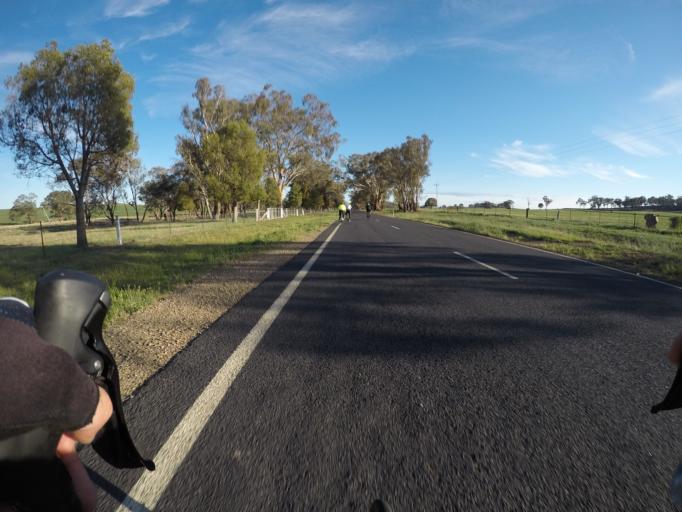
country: AU
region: New South Wales
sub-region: Cabonne
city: Molong
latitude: -32.9478
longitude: 148.7620
